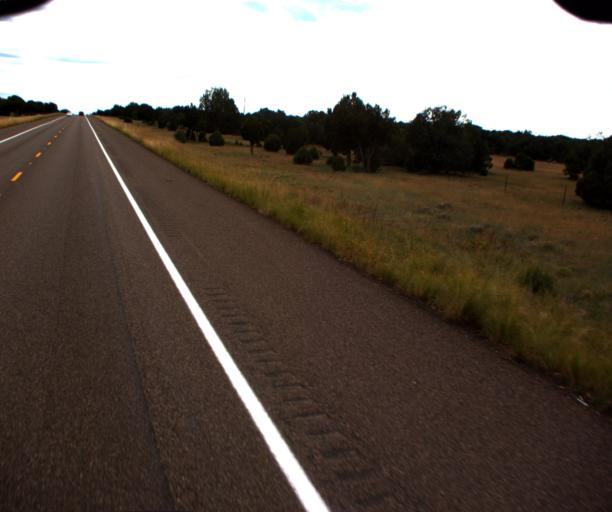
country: US
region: Arizona
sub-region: Navajo County
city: White Mountain Lake
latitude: 34.3148
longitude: -110.0407
